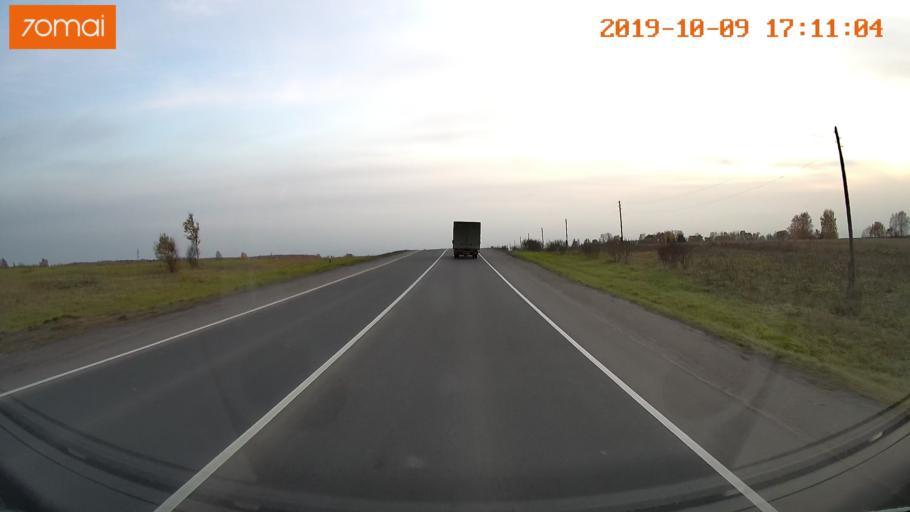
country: RU
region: Ivanovo
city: Privolzhsk
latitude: 57.3474
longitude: 41.2526
